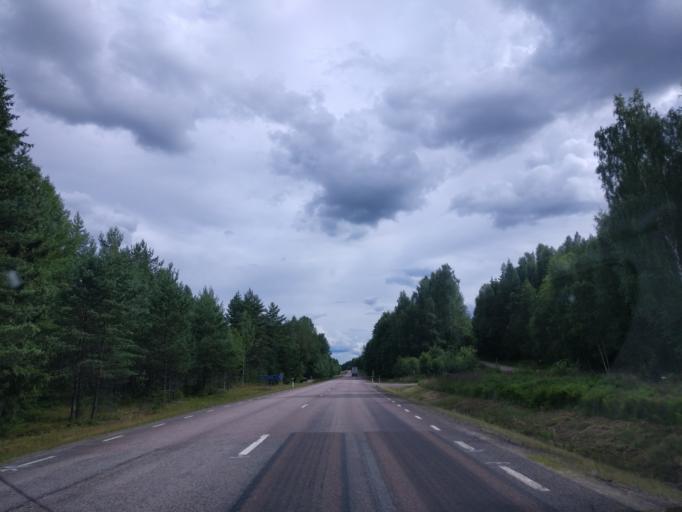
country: SE
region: Vaermland
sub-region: Hagfors Kommun
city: Ekshaerad
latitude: 60.1554
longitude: 13.5164
